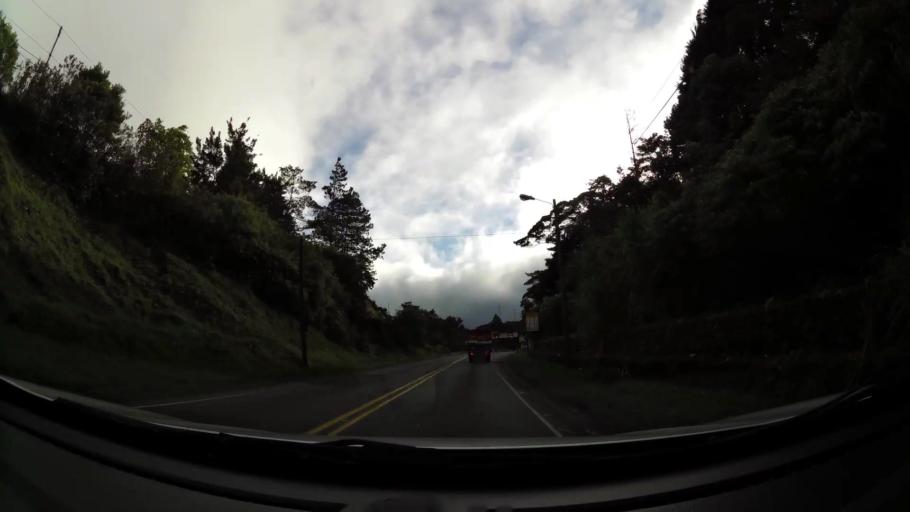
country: CR
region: Heredia
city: Angeles
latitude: 10.0305
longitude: -84.0090
